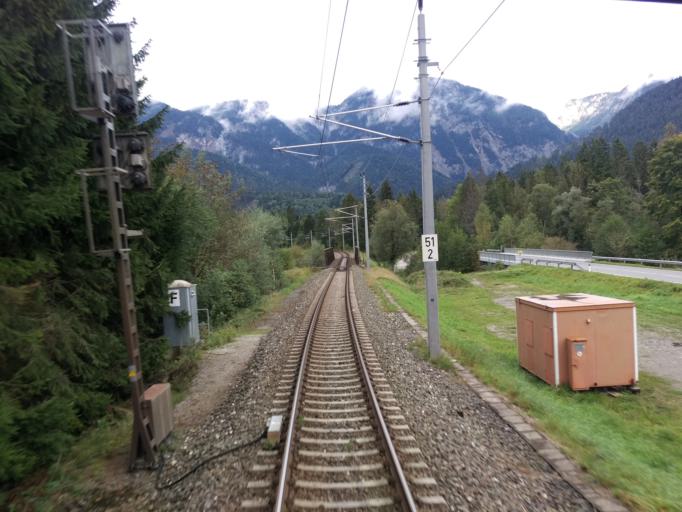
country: AT
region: Styria
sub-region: Politischer Bezirk Liezen
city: Aich
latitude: 47.4194
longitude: 13.7935
